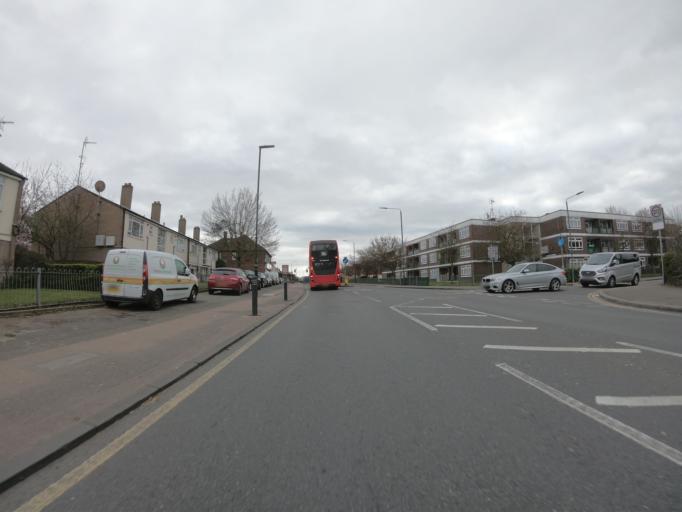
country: GB
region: England
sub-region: Greater London
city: Welling
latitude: 51.4714
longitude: 0.1108
